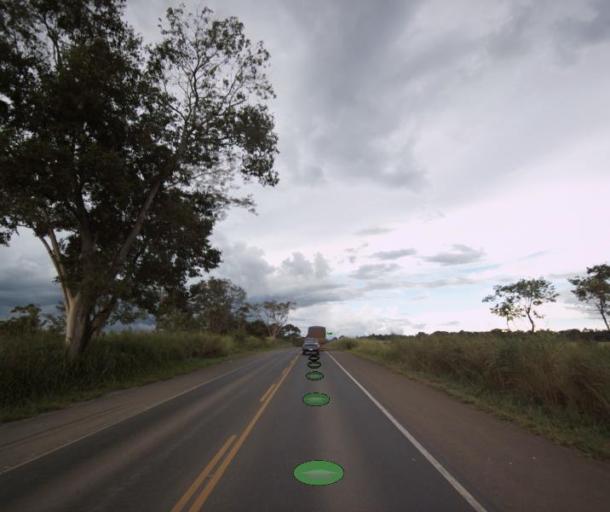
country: BR
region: Goias
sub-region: Itapaci
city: Itapaci
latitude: -15.0487
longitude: -49.4441
